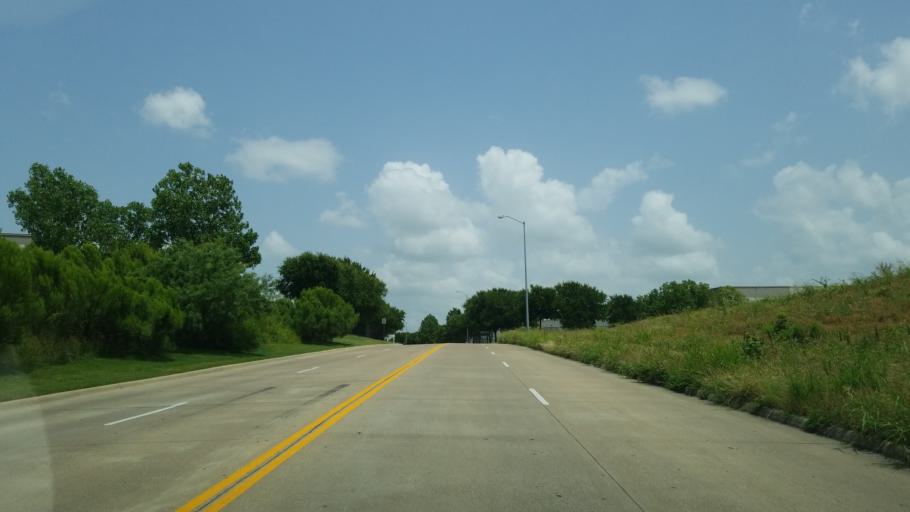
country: US
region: Texas
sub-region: Dallas County
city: Cockrell Hill
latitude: 32.7601
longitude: -96.8891
